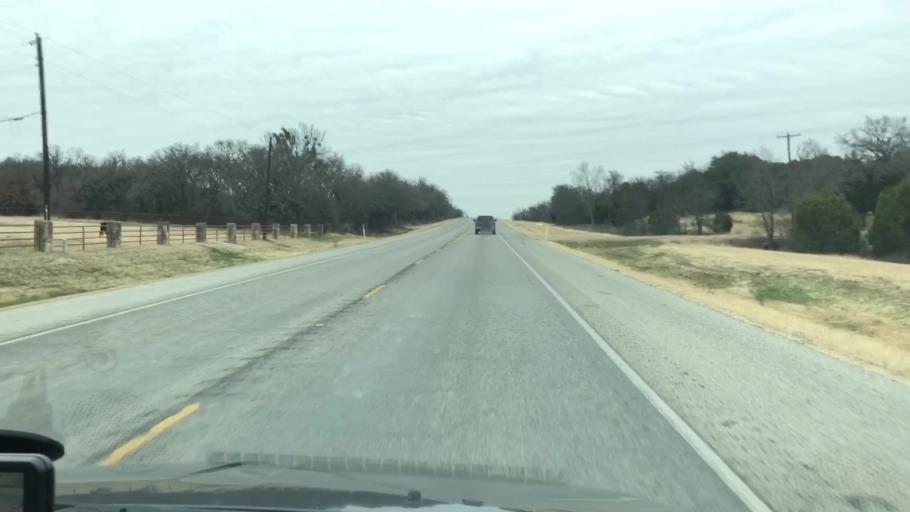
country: US
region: Texas
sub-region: Palo Pinto County
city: Mineral Wells
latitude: 32.8443
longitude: -98.1020
